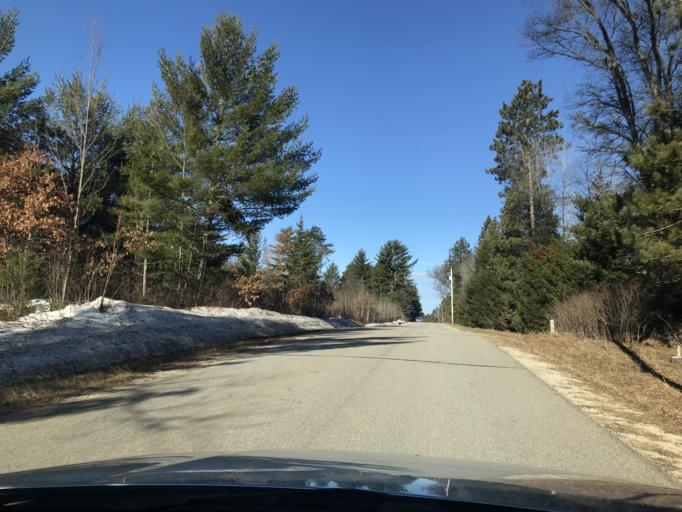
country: US
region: Wisconsin
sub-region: Marinette County
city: Niagara
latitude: 45.3986
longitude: -88.0936
